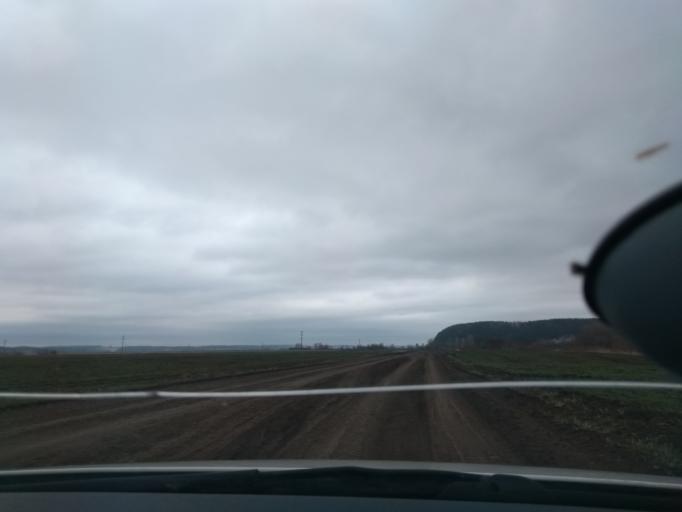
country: RU
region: Perm
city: Orda
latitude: 57.2550
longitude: 56.6262
